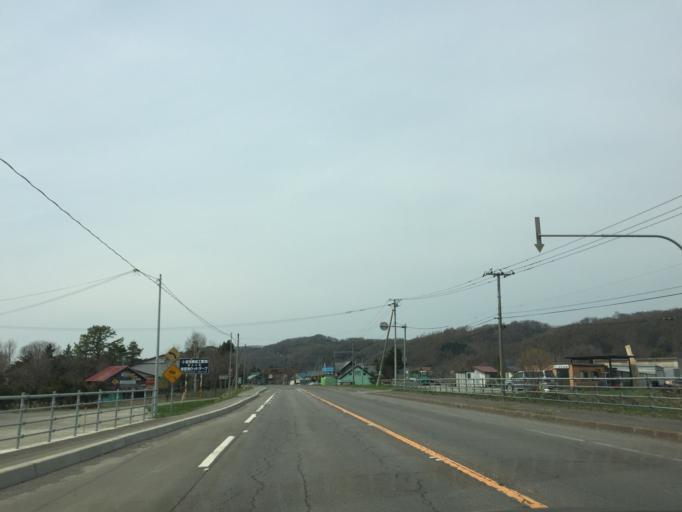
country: JP
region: Hokkaido
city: Ashibetsu
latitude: 43.5416
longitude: 142.1333
